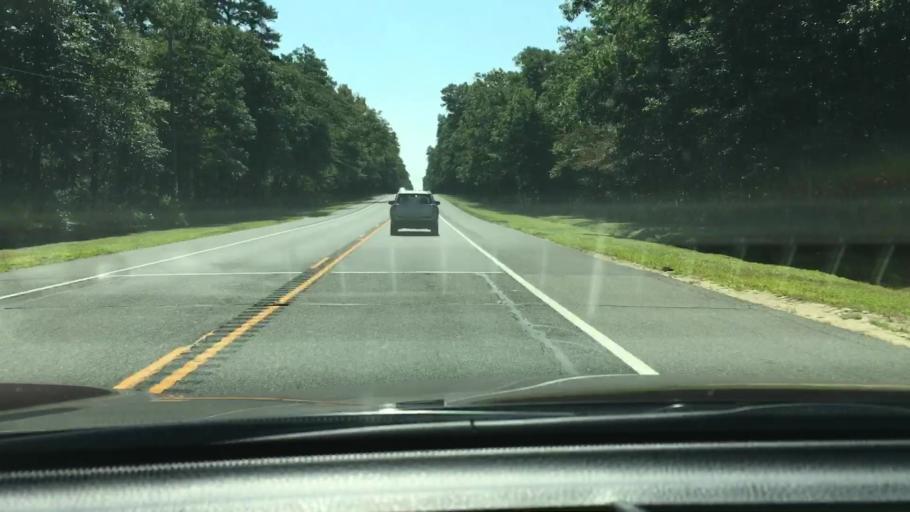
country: US
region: New Jersey
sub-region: Cumberland County
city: Laurel Lake
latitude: 39.3494
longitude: -74.9072
